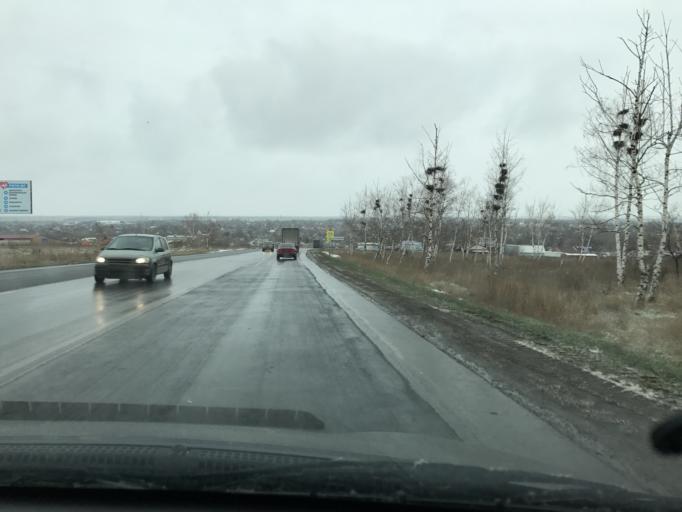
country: RU
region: Rostov
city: Kagal'nitskaya
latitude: 46.8887
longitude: 40.1381
